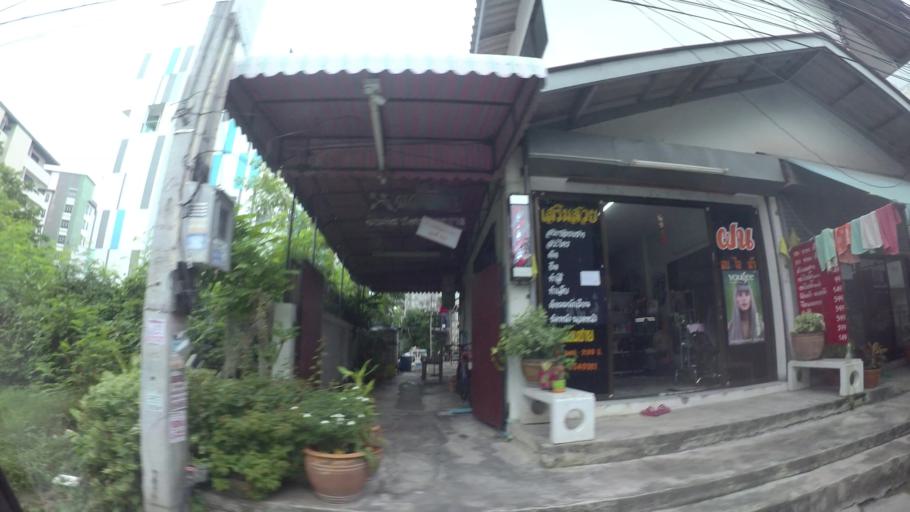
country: TH
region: Chon Buri
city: Bang Lamung
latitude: 13.0797
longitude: 100.9197
